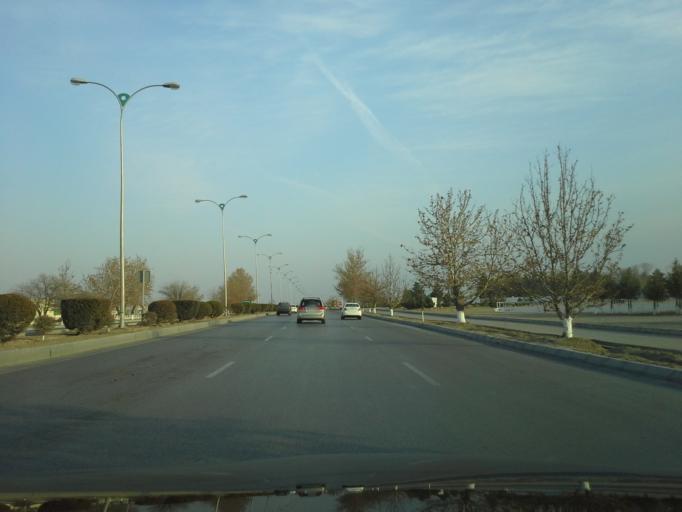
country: TM
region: Ahal
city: Abadan
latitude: 38.0582
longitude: 58.1763
